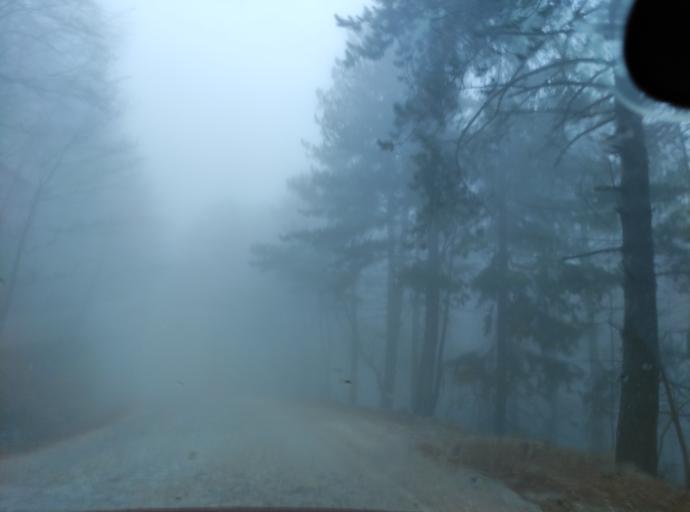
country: BG
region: Sofia-Capital
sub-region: Stolichna Obshtina
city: Sofia
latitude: 42.6179
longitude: 23.2952
